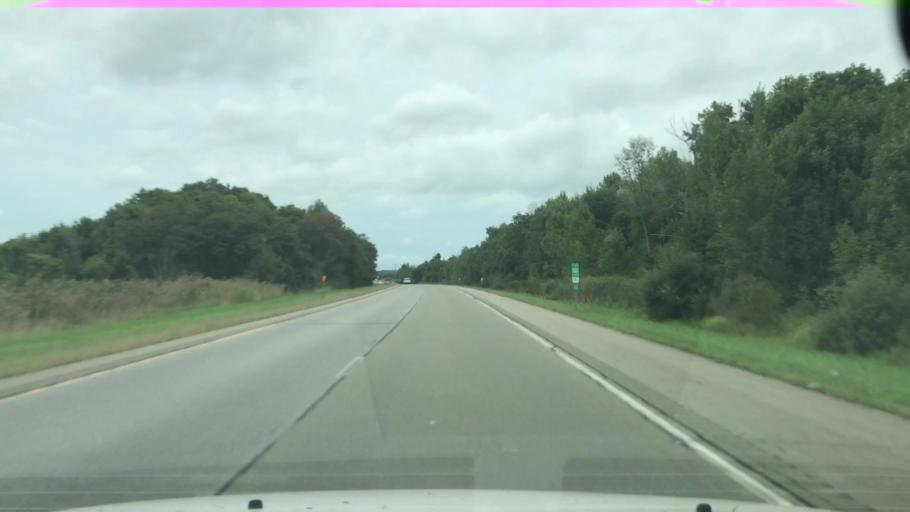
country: US
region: New York
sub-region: Erie County
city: North Boston
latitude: 42.6103
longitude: -78.7589
